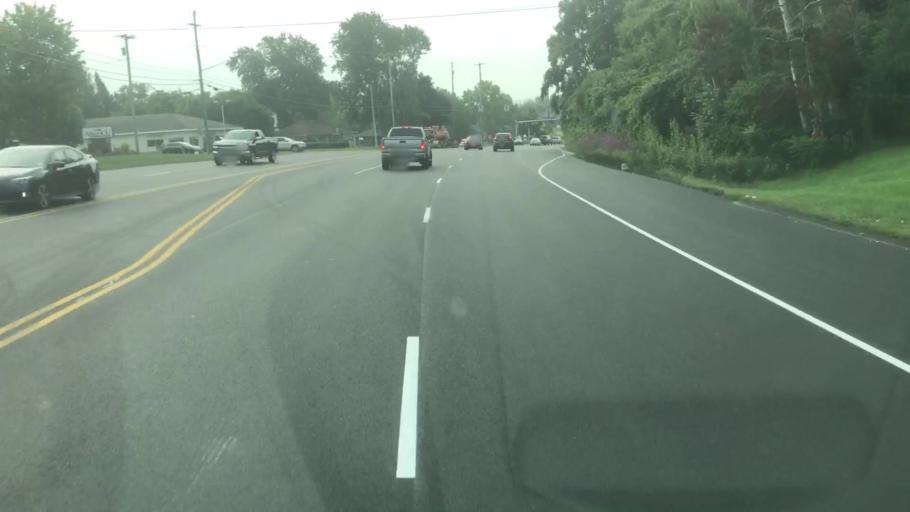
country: US
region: New York
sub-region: Onondaga County
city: Liverpool
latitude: 43.1330
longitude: -76.2213
